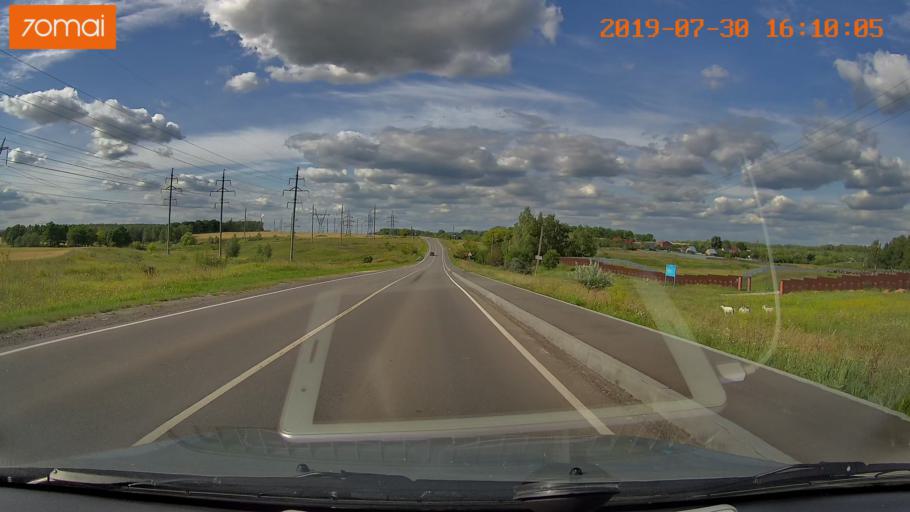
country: RU
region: Moskovskaya
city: Peski
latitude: 55.2591
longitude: 38.7155
